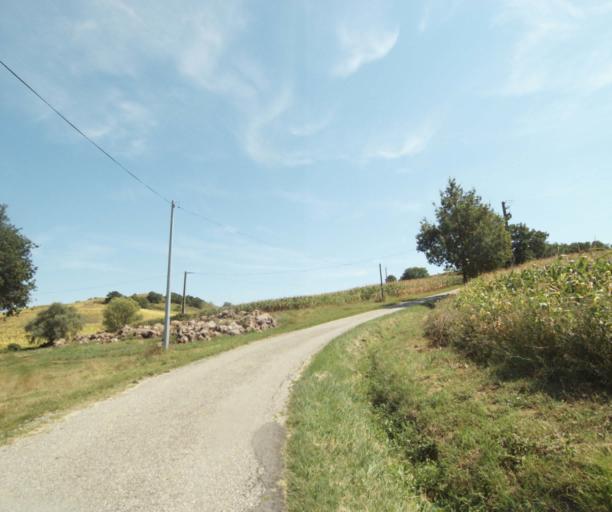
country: FR
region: Midi-Pyrenees
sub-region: Departement de l'Ariege
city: Lezat-sur-Leze
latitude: 43.2525
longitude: 1.3794
